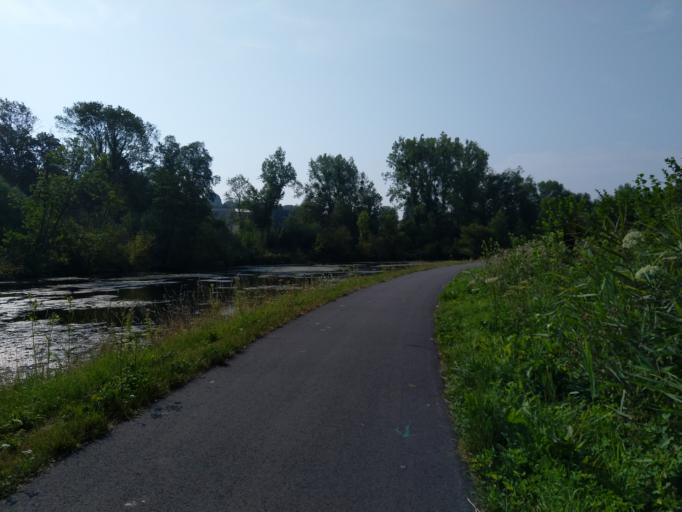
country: BE
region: Wallonia
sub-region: Province du Hainaut
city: Seneffe
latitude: 50.5867
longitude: 4.2544
